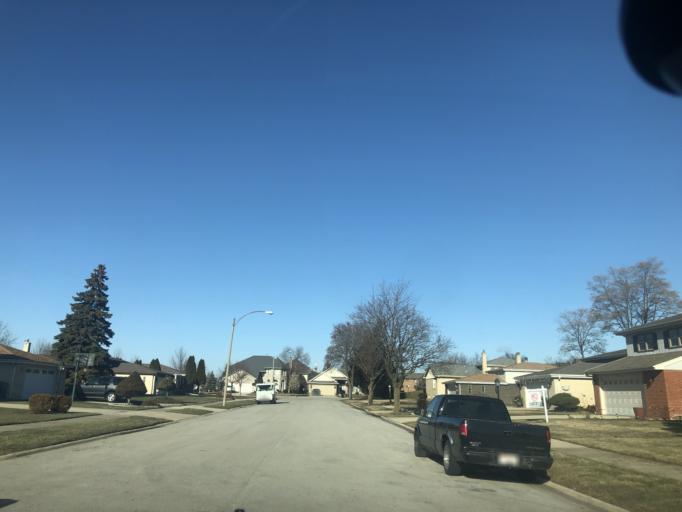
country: US
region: Illinois
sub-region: DuPage County
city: Addison
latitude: 41.9351
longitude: -88.0076
